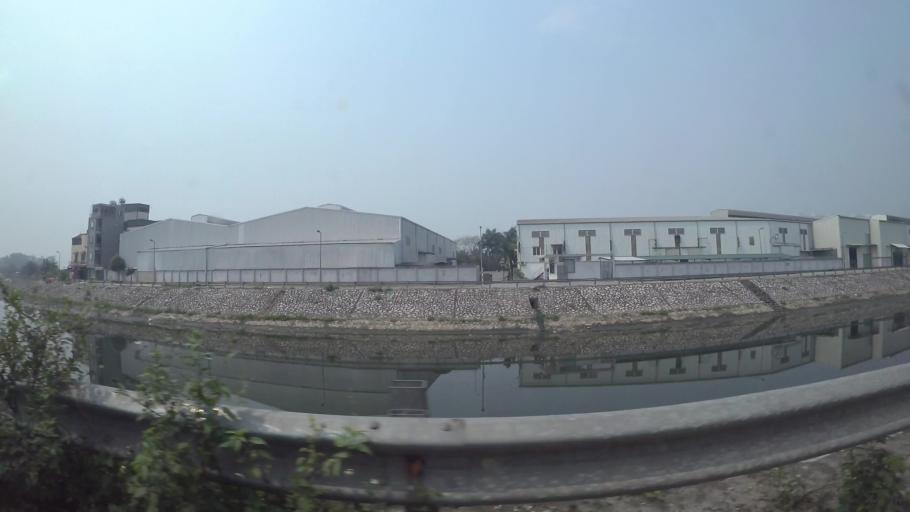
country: VN
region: Ha Noi
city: Van Dien
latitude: 20.9598
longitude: 105.8178
